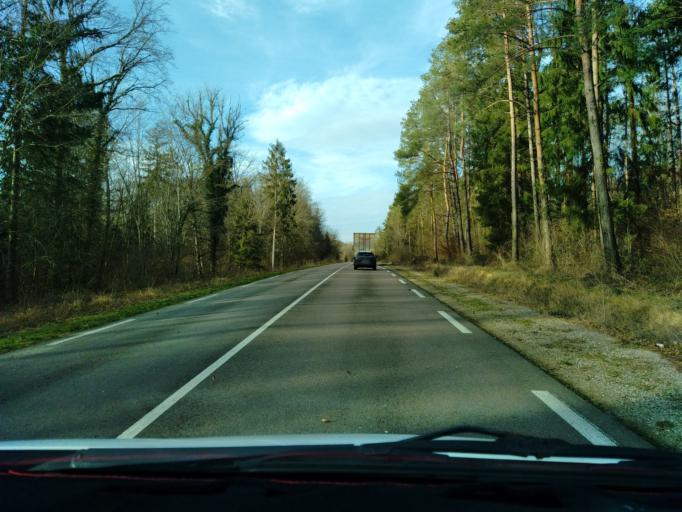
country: FR
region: Franche-Comte
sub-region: Departement de la Haute-Saone
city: Gray
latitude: 47.4019
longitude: 5.6422
